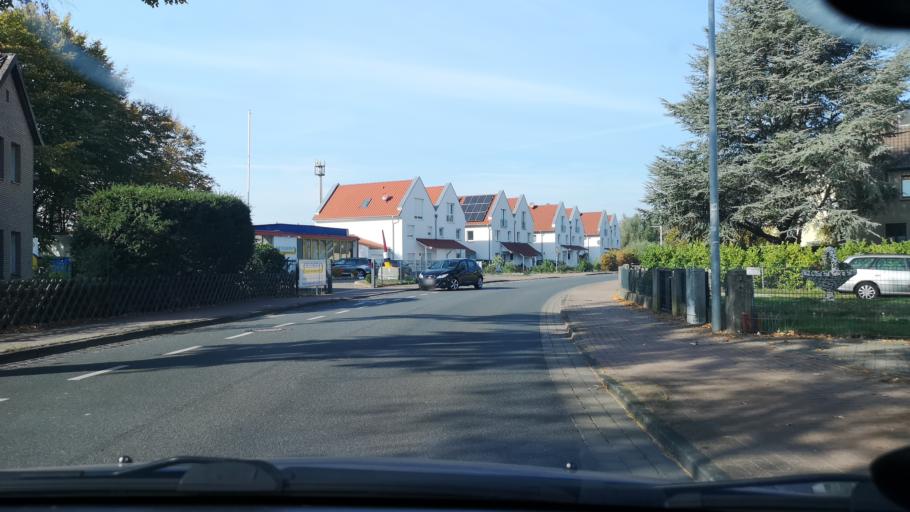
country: DE
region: Lower Saxony
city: Auf der Horst
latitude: 52.4067
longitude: 9.6061
